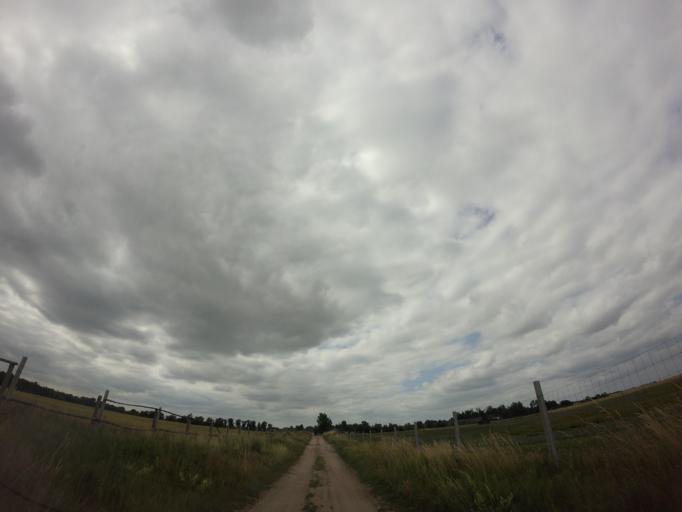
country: PL
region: Lubusz
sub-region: Powiat strzelecko-drezdenecki
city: Strzelce Krajenskie
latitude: 52.9090
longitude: 15.5994
